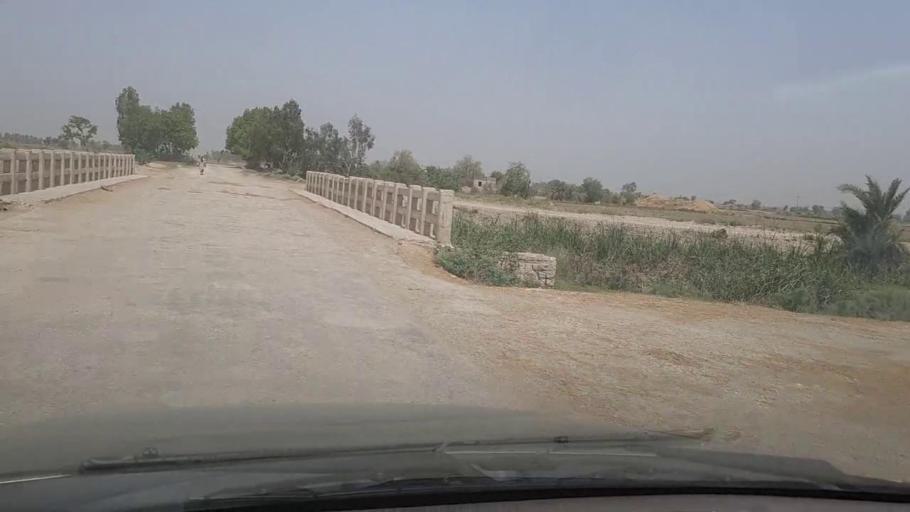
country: PK
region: Sindh
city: Madeji
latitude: 27.8298
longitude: 68.3902
